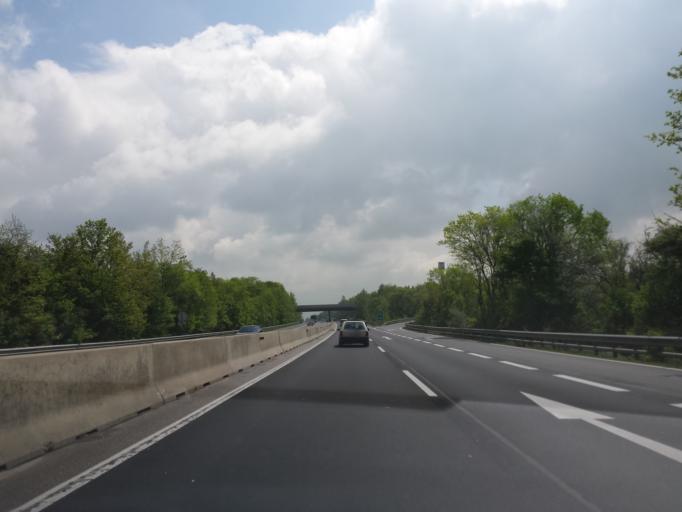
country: AT
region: Lower Austria
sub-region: Politischer Bezirk Bruck an der Leitha
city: Bruck an der Leitha
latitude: 48.0597
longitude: 16.7061
